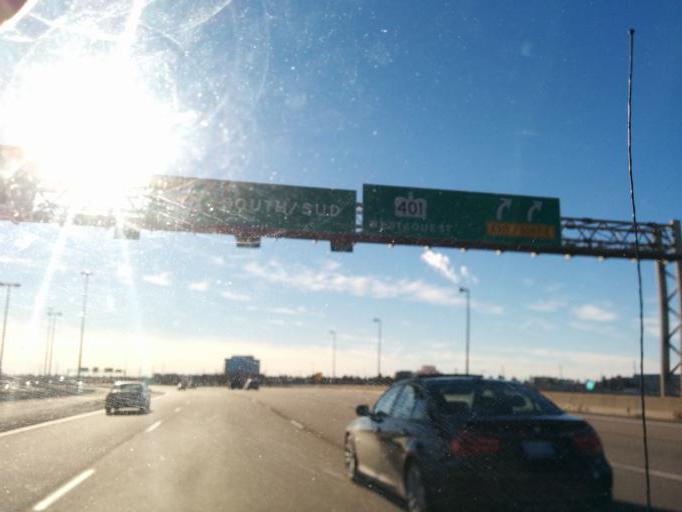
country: CA
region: Ontario
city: Etobicoke
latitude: 43.6758
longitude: -79.5924
